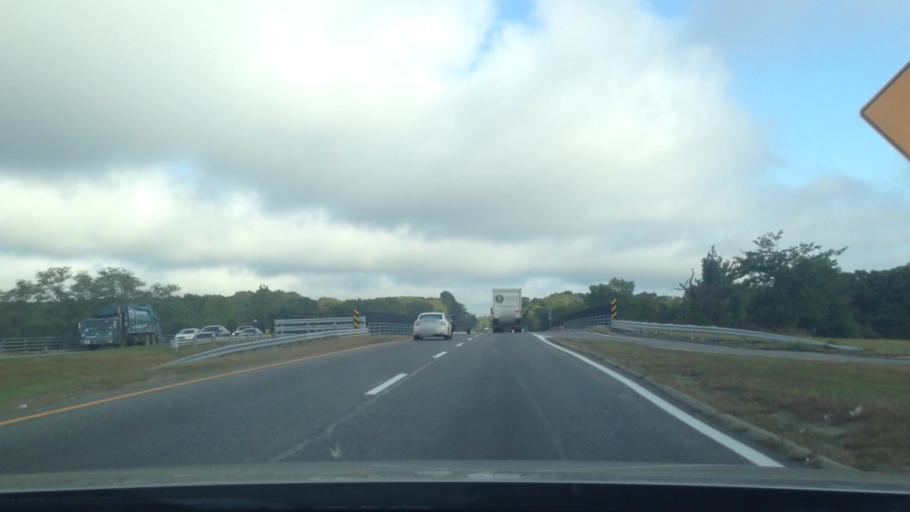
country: US
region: New York
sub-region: Suffolk County
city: Holtsville
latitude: 40.8347
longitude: -73.0564
